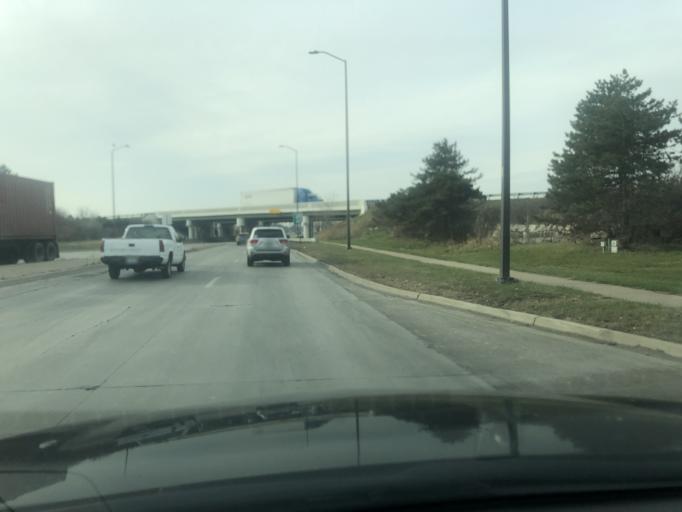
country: US
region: Michigan
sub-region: Wayne County
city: Southgate
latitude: 42.2133
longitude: -83.2205
